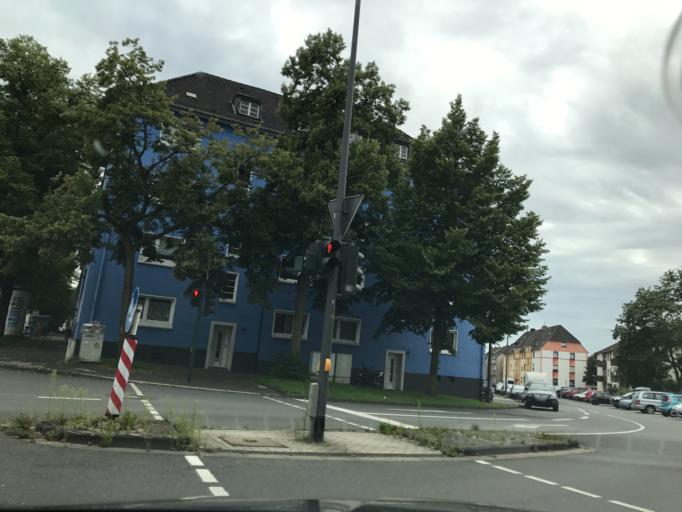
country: DE
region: North Rhine-Westphalia
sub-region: Regierungsbezirk Munster
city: Bottrop
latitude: 51.4808
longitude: 6.9620
